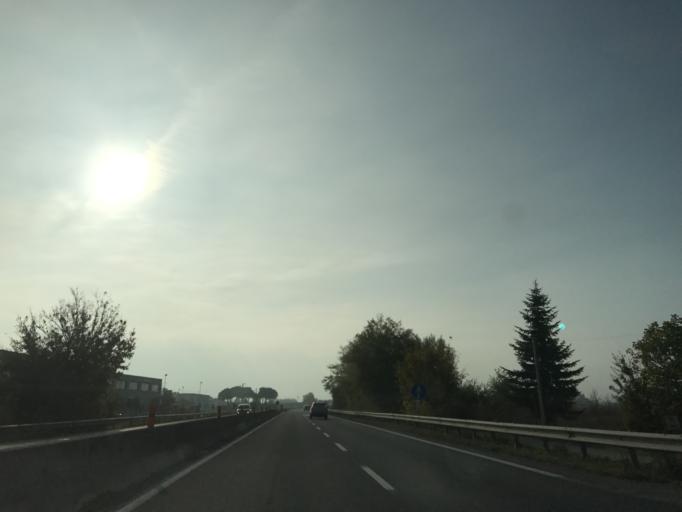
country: IT
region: Emilia-Romagna
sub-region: Provincia di Rimini
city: Bellaria-Igea Marina
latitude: 44.1306
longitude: 12.4667
